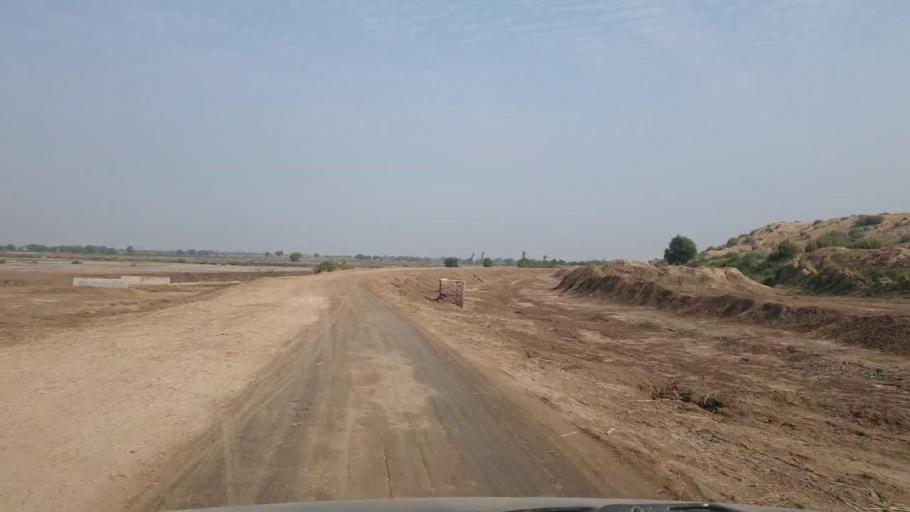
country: PK
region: Sindh
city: Tando Muhammad Khan
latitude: 25.1483
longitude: 68.4595
